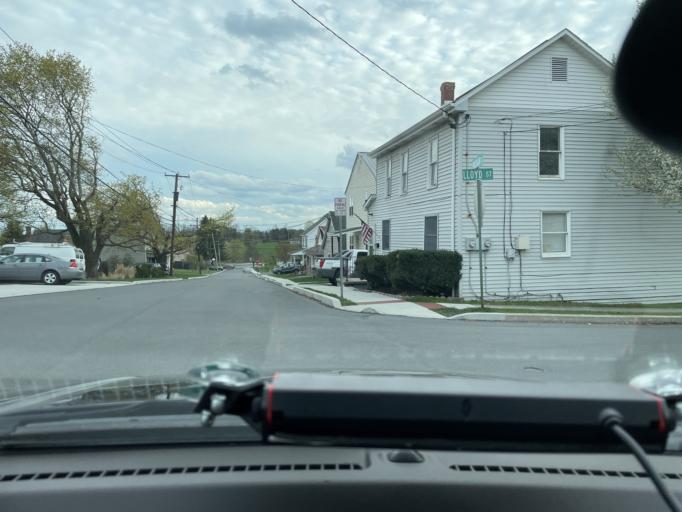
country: US
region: Pennsylvania
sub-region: Cambria County
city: Ebensburg
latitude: 40.4844
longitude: -78.7293
